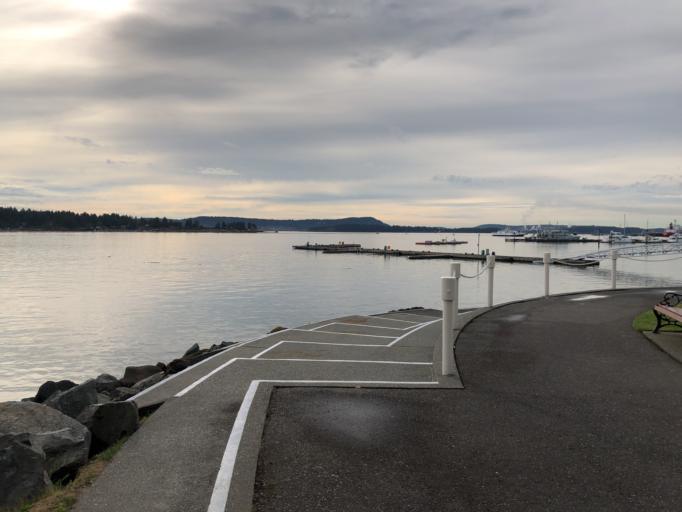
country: CA
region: British Columbia
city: Nanaimo
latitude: 49.1716
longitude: -123.9370
